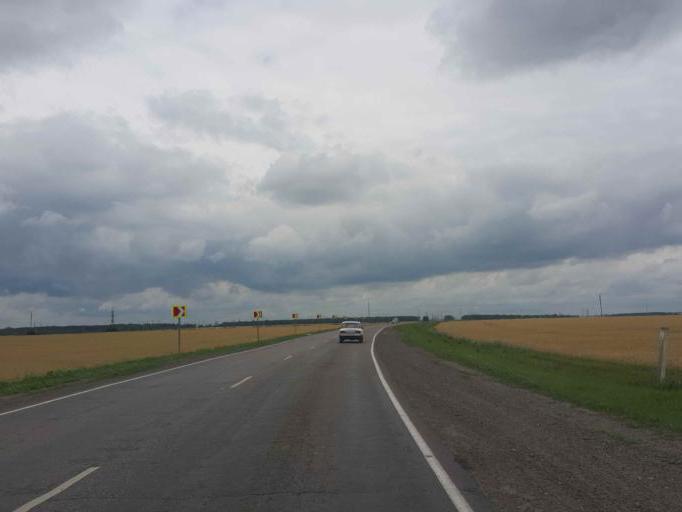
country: RU
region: Tambov
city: Komsomolets
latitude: 52.7521
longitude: 41.2979
